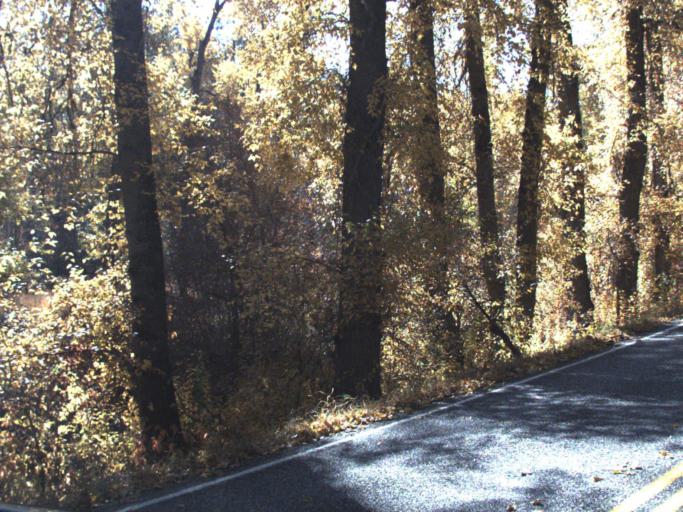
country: CA
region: British Columbia
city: Grand Forks
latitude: 48.9880
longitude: -118.5132
